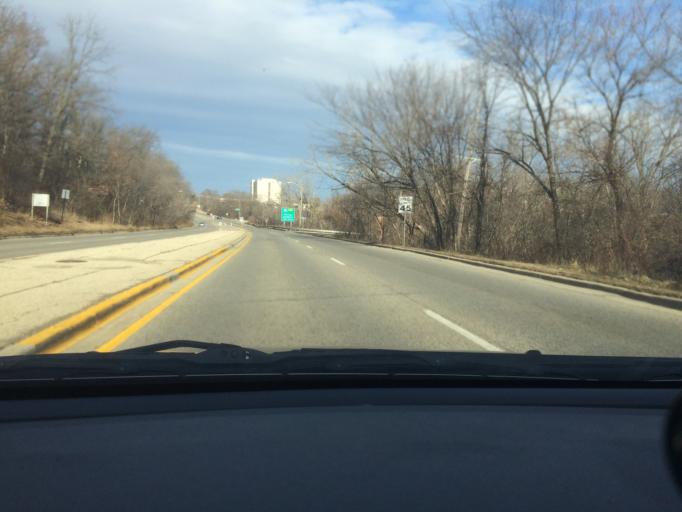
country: US
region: Illinois
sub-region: Kane County
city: Elgin
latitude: 42.0599
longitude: -88.2938
